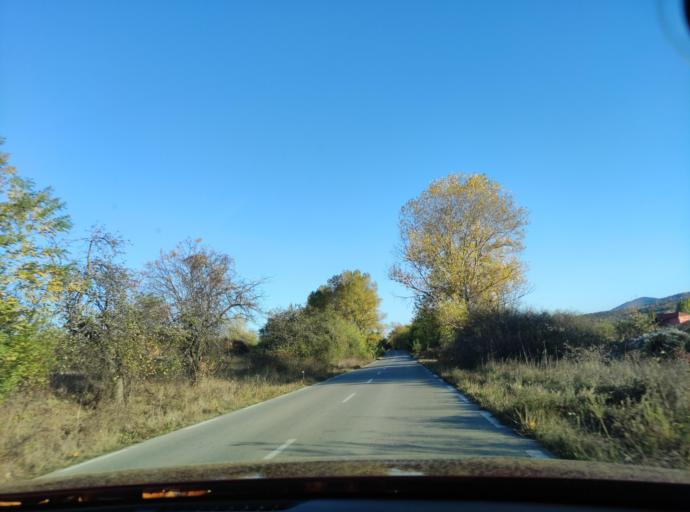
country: BG
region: Montana
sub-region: Obshtina Chiprovtsi
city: Chiprovtsi
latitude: 43.4306
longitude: 22.9932
